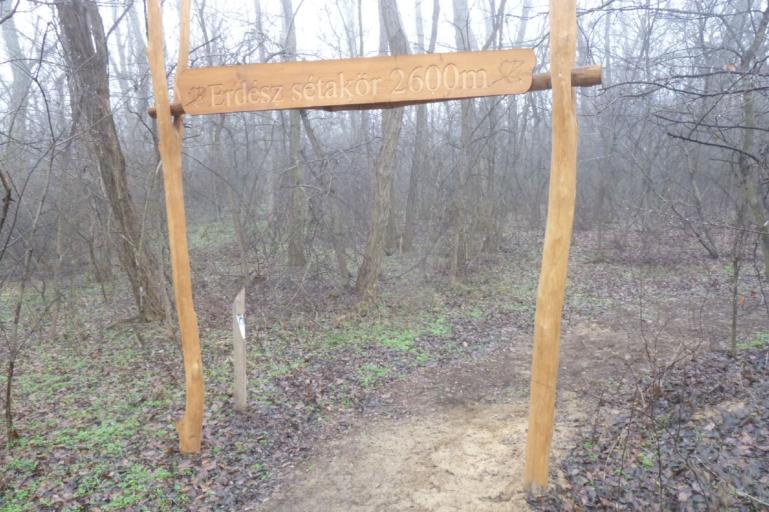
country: HU
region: Pest
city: Kakucs
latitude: 47.2829
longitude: 19.4135
